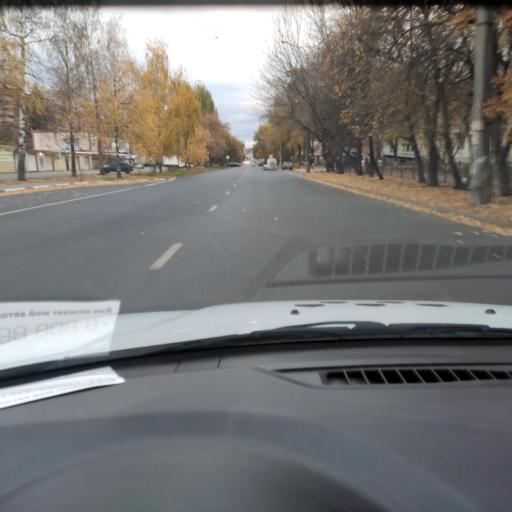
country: RU
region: Samara
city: Tol'yatti
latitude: 53.5268
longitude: 49.4296
